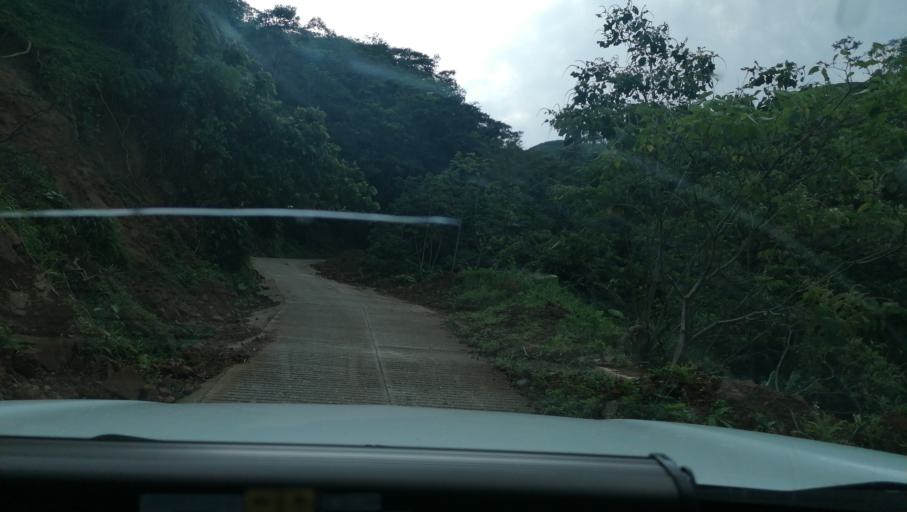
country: MX
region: Chiapas
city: Ixtacomitan
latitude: 17.3350
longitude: -93.1083
